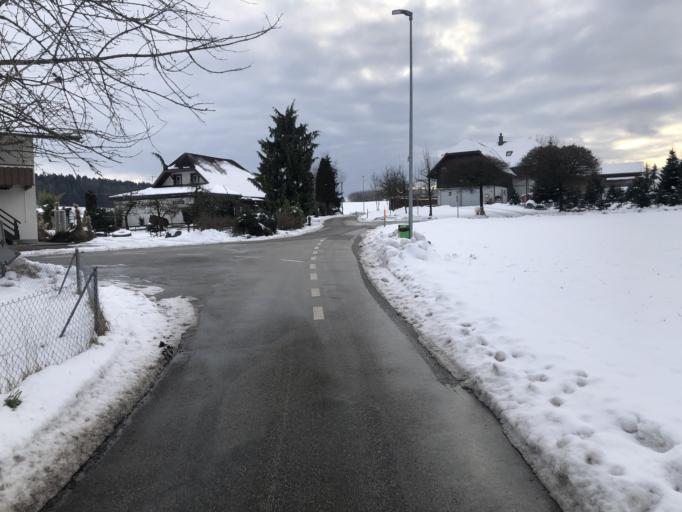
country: CH
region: Bern
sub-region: Oberaargau
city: Herzogenbuchsee
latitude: 47.2032
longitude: 7.7445
